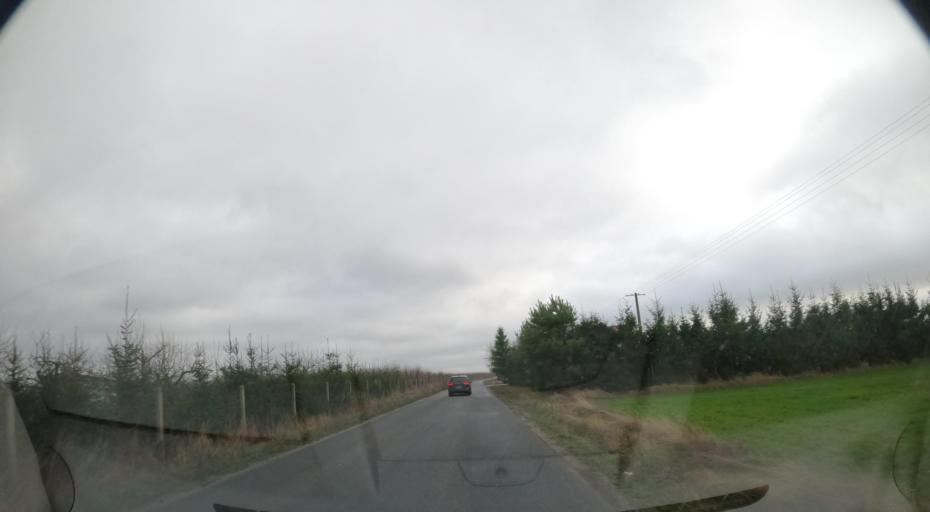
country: PL
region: Greater Poland Voivodeship
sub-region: Powiat pilski
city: Lobzenica
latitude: 53.2452
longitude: 17.2926
